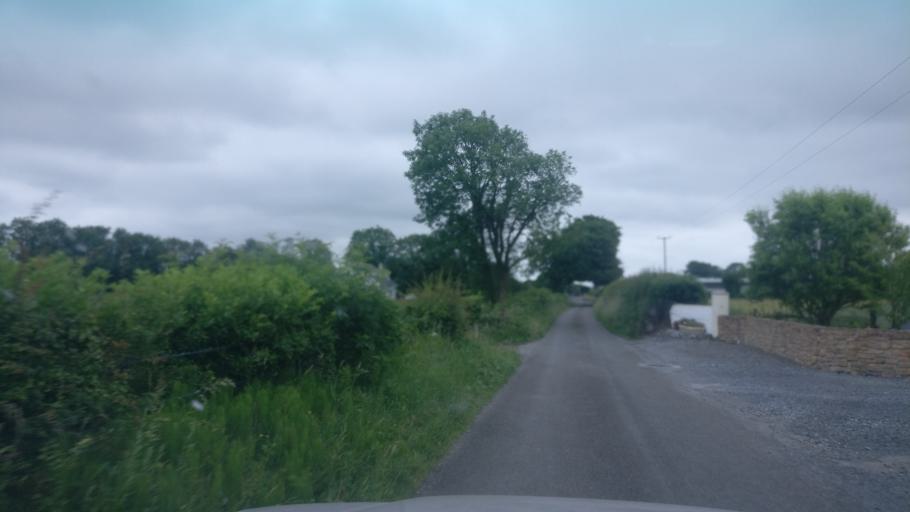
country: IE
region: Connaught
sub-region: County Galway
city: Ballinasloe
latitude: 53.2945
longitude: -8.3402
